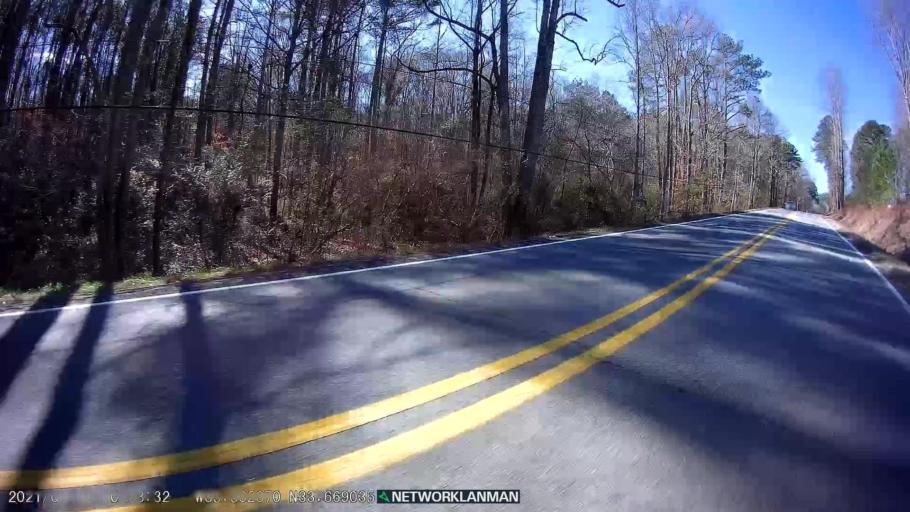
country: US
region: Alabama
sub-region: Cleburne County
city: Heflin
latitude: 33.6689
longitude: -85.5628
